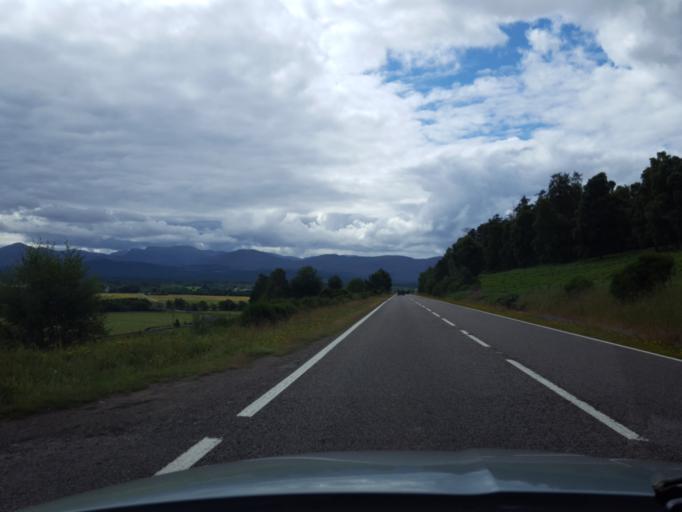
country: GB
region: Scotland
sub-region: Highland
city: Grantown on Spey
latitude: 57.2880
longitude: -3.6671
